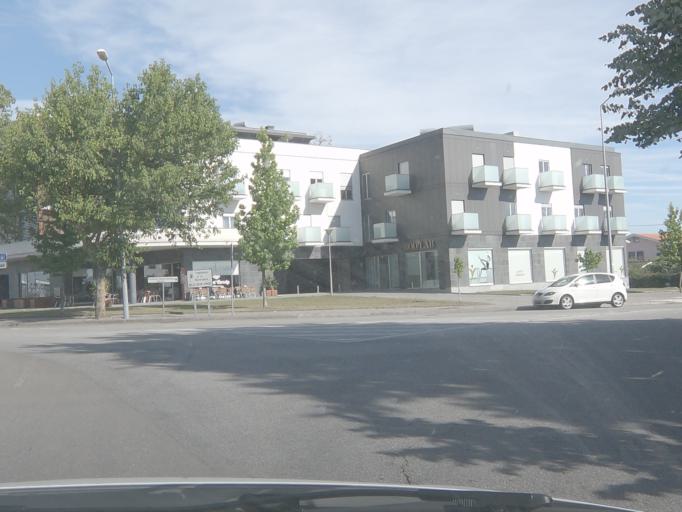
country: PT
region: Viseu
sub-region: Viseu
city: Viseu
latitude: 40.6412
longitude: -7.9182
